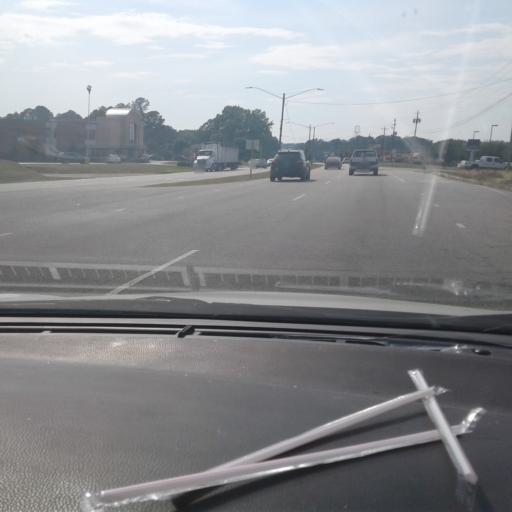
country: US
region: North Carolina
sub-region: Harnett County
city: Dunn
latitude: 35.3200
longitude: -78.6330
